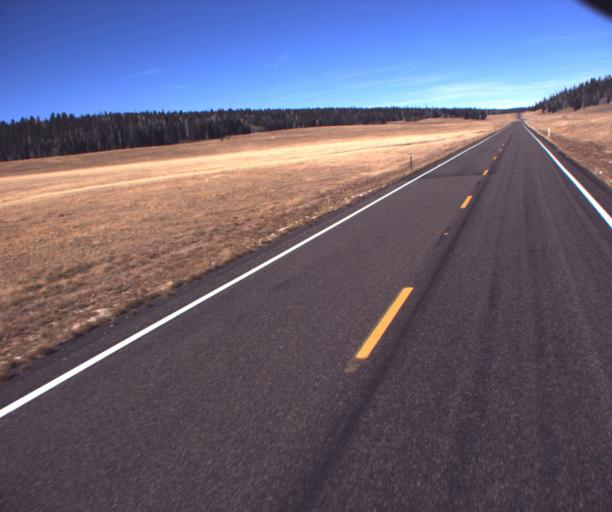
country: US
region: Arizona
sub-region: Coconino County
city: Grand Canyon
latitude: 36.3941
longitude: -112.1279
